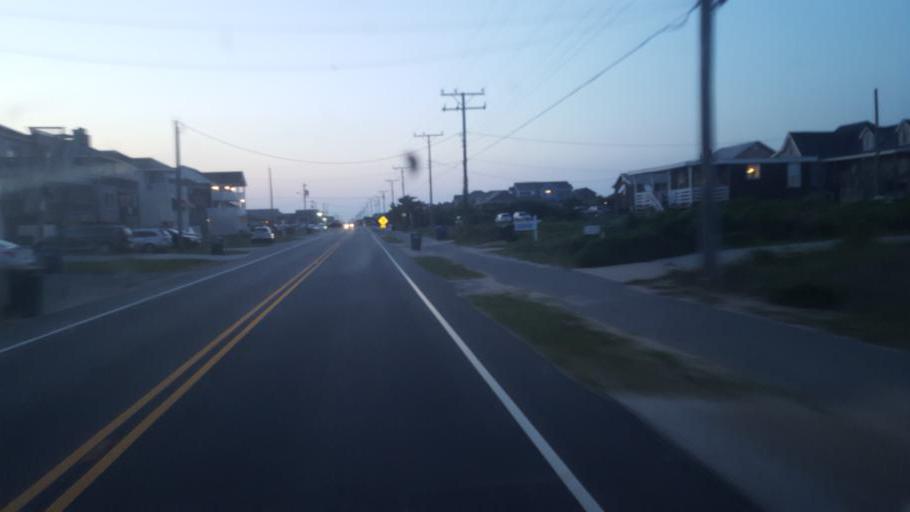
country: US
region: North Carolina
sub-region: Dare County
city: Nags Head
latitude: 35.9768
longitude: -75.6351
